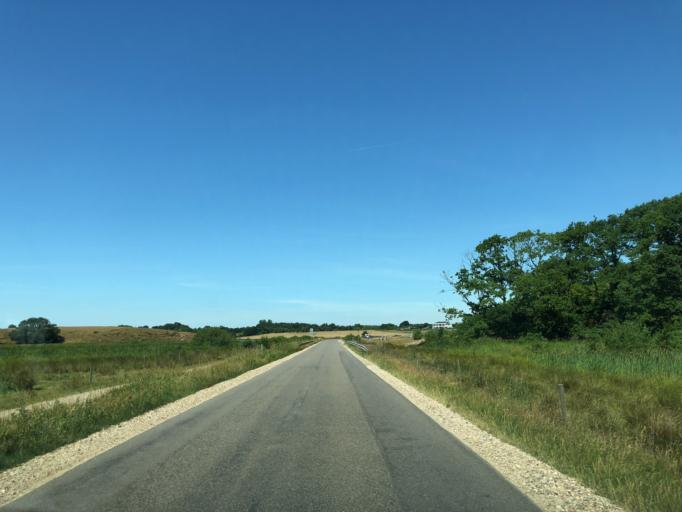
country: DK
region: Central Jutland
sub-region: Holstebro Kommune
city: Holstebro
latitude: 56.3512
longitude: 8.6844
